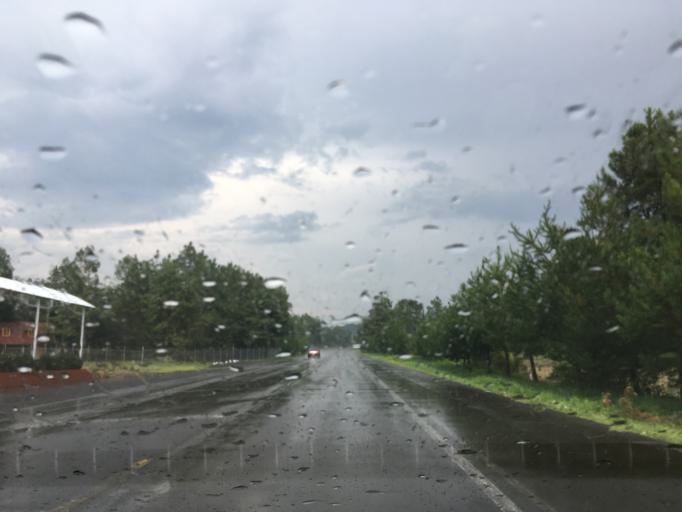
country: MX
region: Michoacan
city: Angahuan
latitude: 19.5705
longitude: -102.2656
